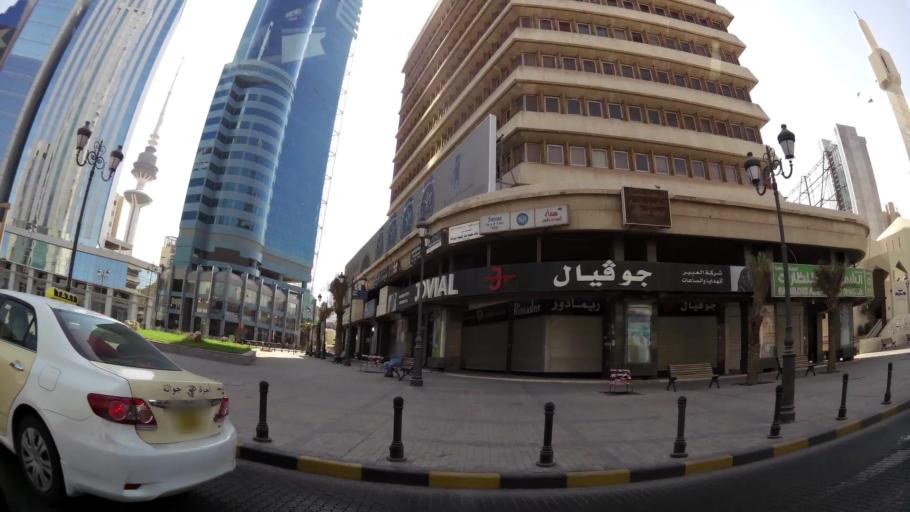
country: KW
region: Al Asimah
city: Kuwait City
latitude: 29.3686
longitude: 47.9690
